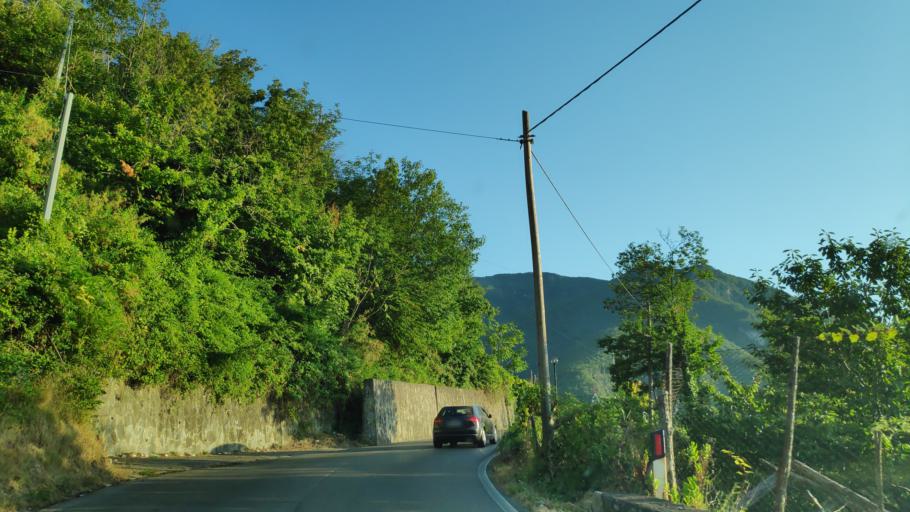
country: IT
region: Campania
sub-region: Provincia di Salerno
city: Corbara
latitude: 40.7235
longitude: 14.5999
